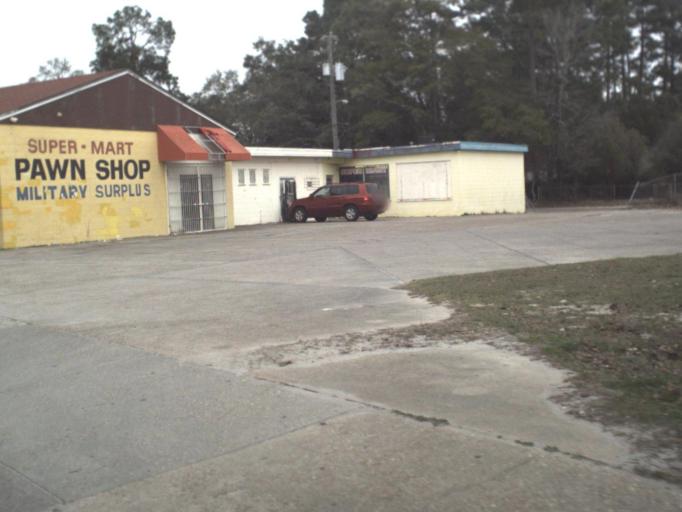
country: US
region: Florida
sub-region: Bay County
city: Springfield
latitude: 30.1562
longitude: -85.6215
